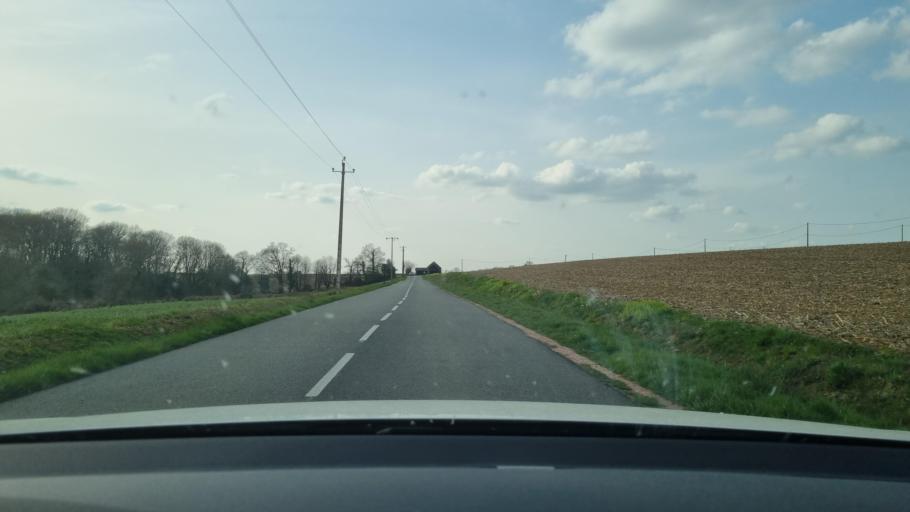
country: FR
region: Aquitaine
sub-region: Departement des Pyrenees-Atlantiques
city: Ger
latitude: 43.3739
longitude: -0.0847
